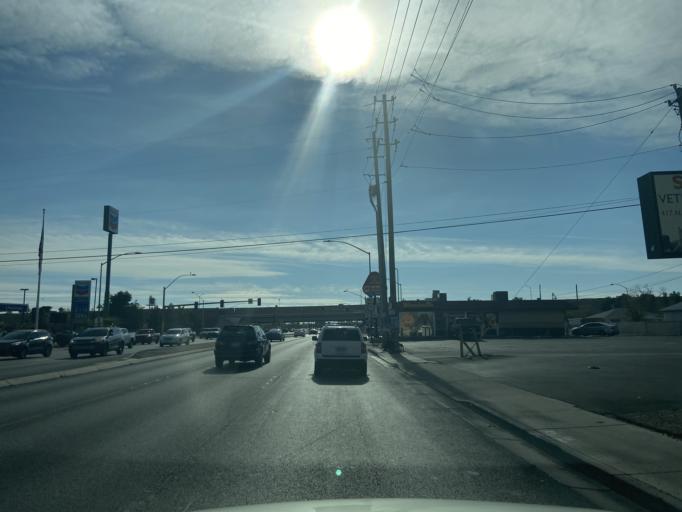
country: US
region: Nevada
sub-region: Clark County
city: Las Vegas
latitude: 36.1701
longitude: -115.1161
